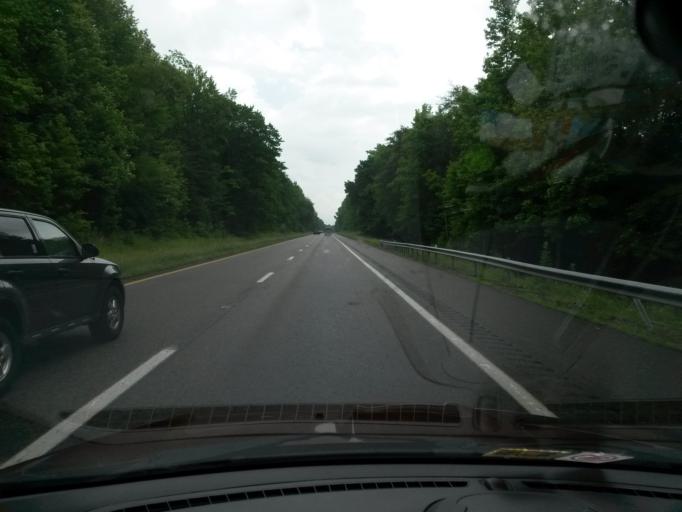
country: US
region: Virginia
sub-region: Goochland County
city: Goochland
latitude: 37.7507
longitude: -77.8488
